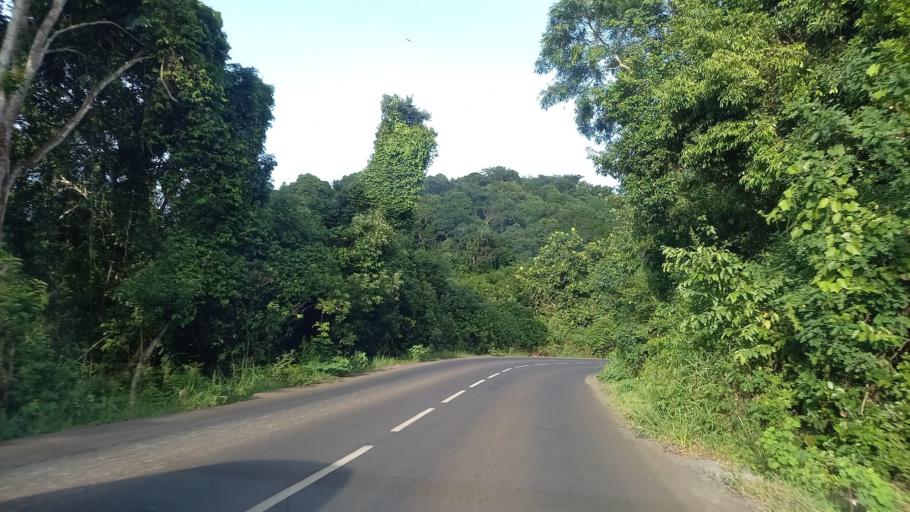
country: YT
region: Bandraboua
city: Bandraboua
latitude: -12.7363
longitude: 45.1186
